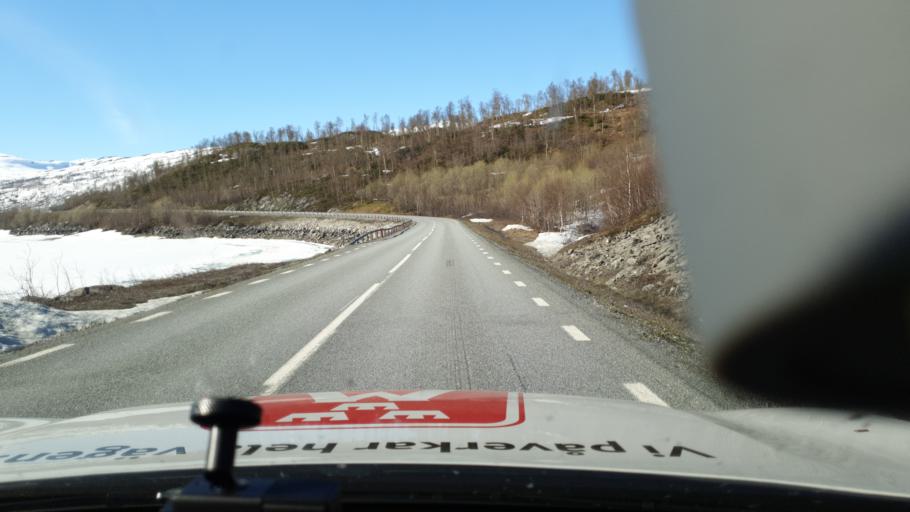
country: NO
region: Nordland
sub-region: Rana
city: Mo i Rana
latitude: 66.1059
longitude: 14.8205
